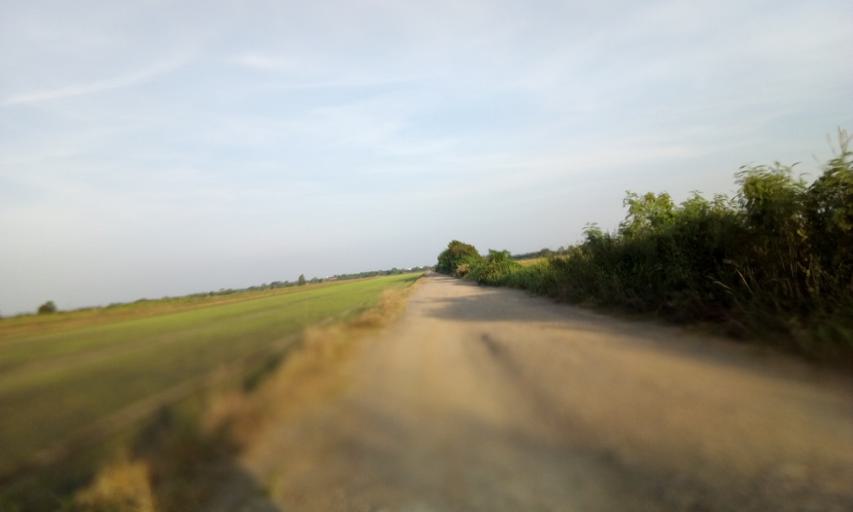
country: TH
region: Pathum Thani
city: Ban Lam Luk Ka
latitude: 14.0355
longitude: 100.8477
